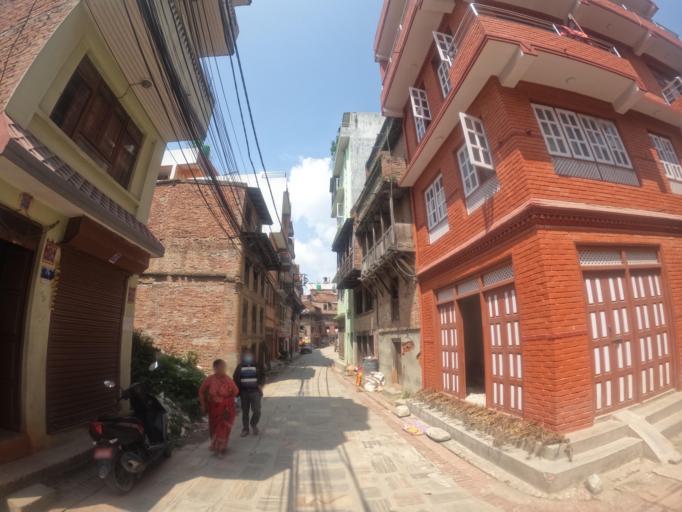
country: NP
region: Central Region
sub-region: Bagmati Zone
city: Bhaktapur
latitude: 27.6907
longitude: 85.3892
